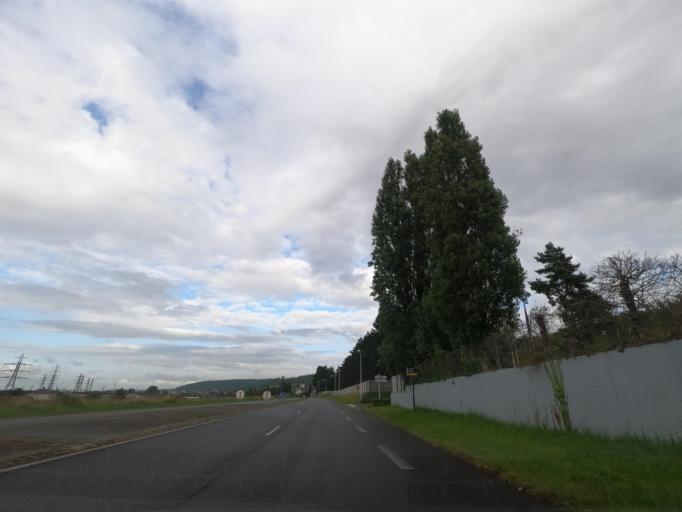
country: FR
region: Haute-Normandie
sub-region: Departement de la Seine-Maritime
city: Grand-Couronne
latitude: 49.3446
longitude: 0.9839
